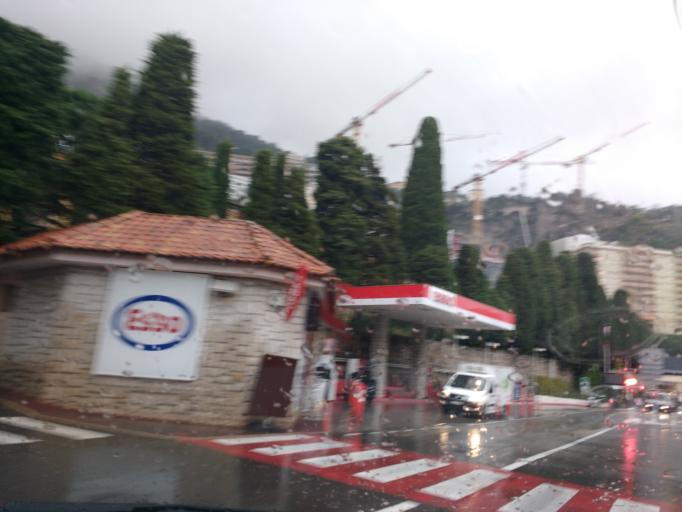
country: MC
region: Commune de Monaco
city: Fontvieille
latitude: 43.7283
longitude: 7.4121
